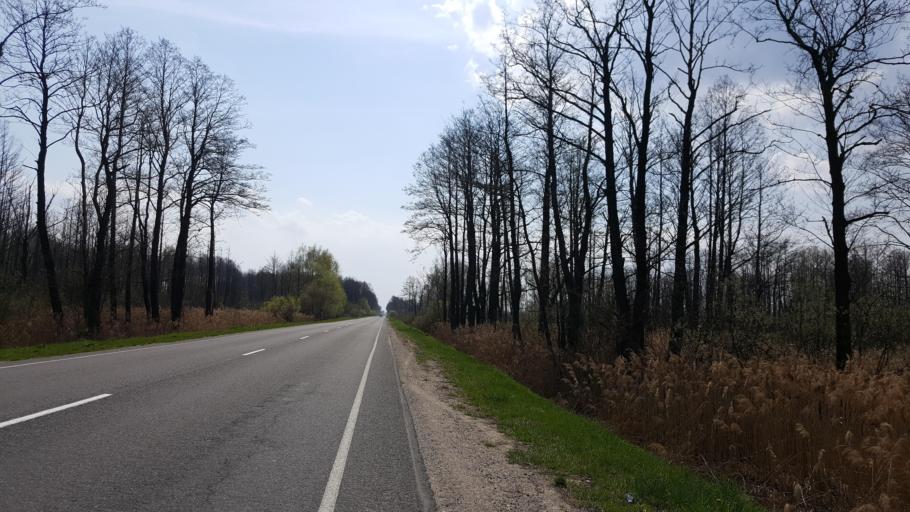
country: BY
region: Brest
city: Zhabinka
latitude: 52.2767
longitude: 23.9511
